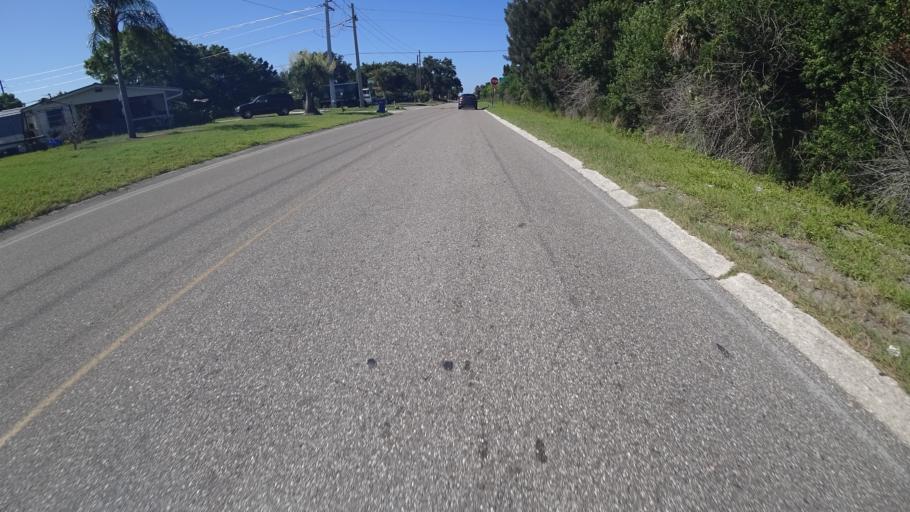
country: US
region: Florida
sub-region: Manatee County
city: Bayshore Gardens
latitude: 27.4257
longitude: -82.5960
